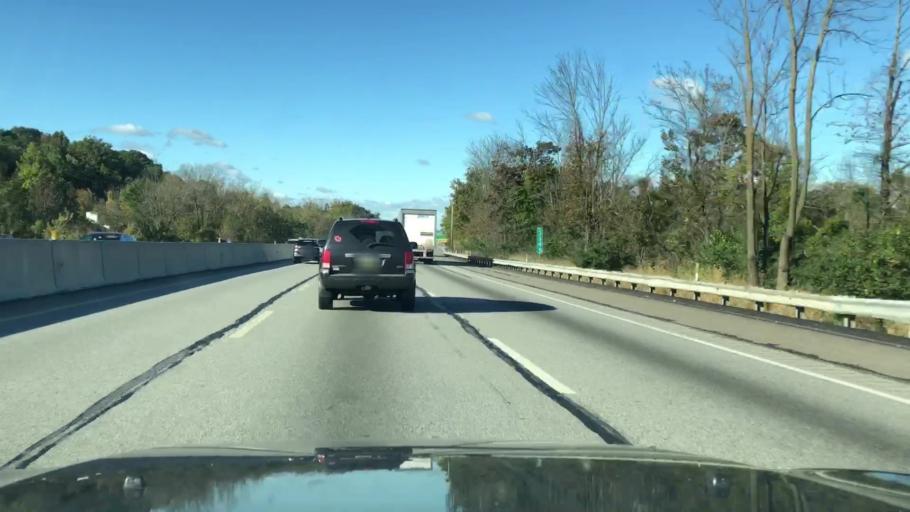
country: US
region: Pennsylvania
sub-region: Montgomery County
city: Plymouth Meeting
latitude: 40.1145
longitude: -75.2650
